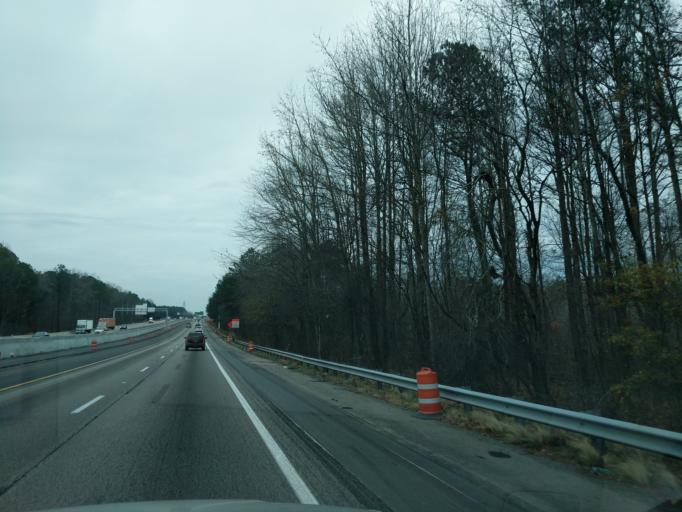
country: US
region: Georgia
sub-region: Gwinnett County
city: Dacula
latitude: 34.0693
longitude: -83.9316
